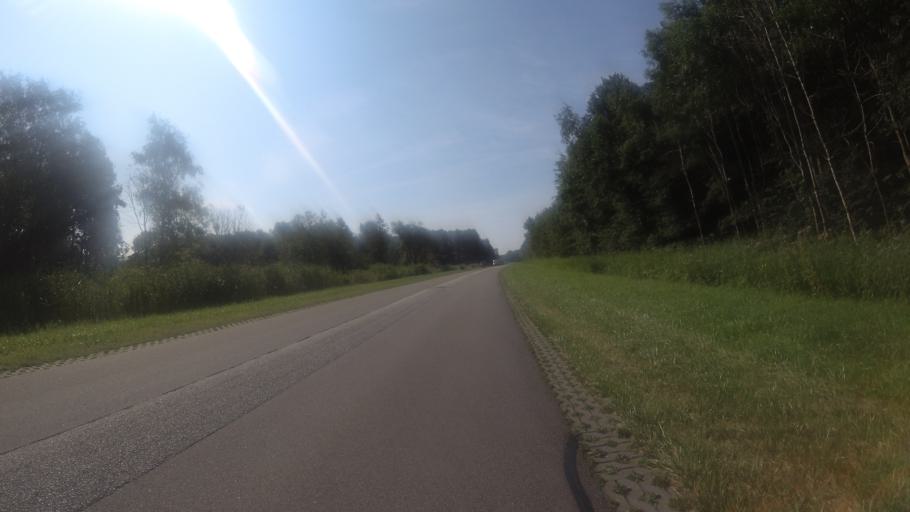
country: NL
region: Zeeland
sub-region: Gemeente Veere
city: Veere
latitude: 51.5814
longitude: 3.6605
